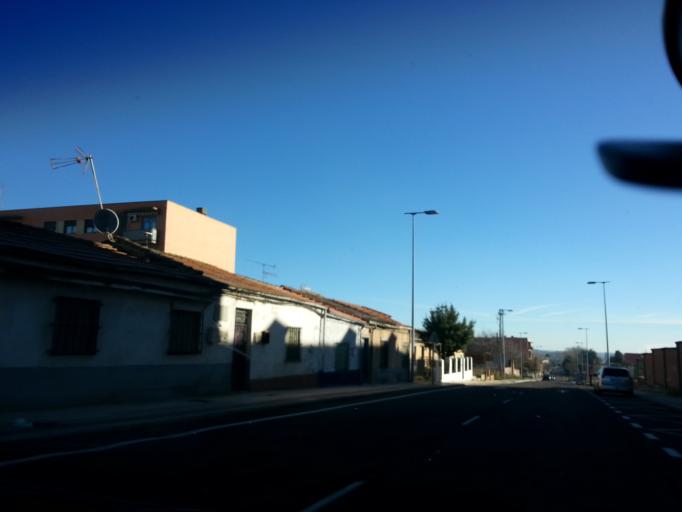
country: ES
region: Castille and Leon
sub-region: Provincia de Salamanca
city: Salamanca
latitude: 40.9692
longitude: -5.6413
